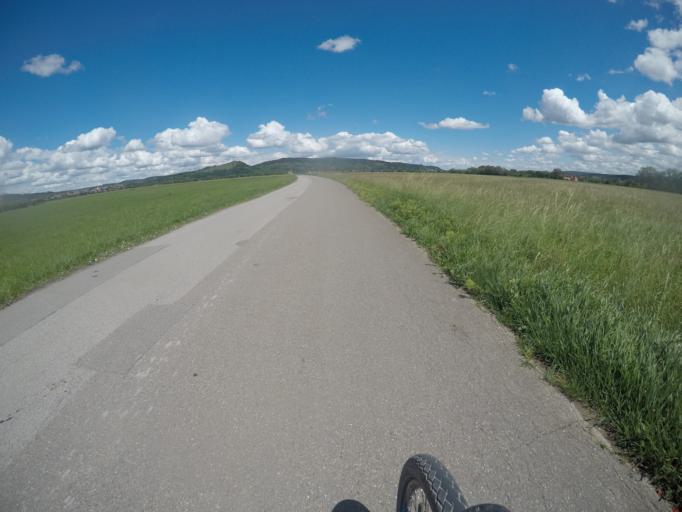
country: DE
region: Baden-Wuerttemberg
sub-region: Tuebingen Region
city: Rottenburg
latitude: 48.4844
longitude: 8.9673
